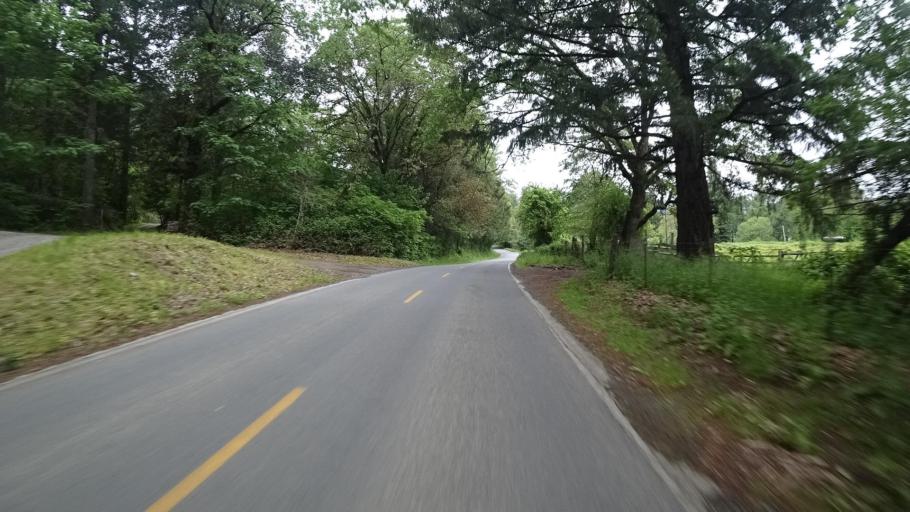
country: US
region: California
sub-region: Humboldt County
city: Willow Creek
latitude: 41.0800
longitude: -123.7005
